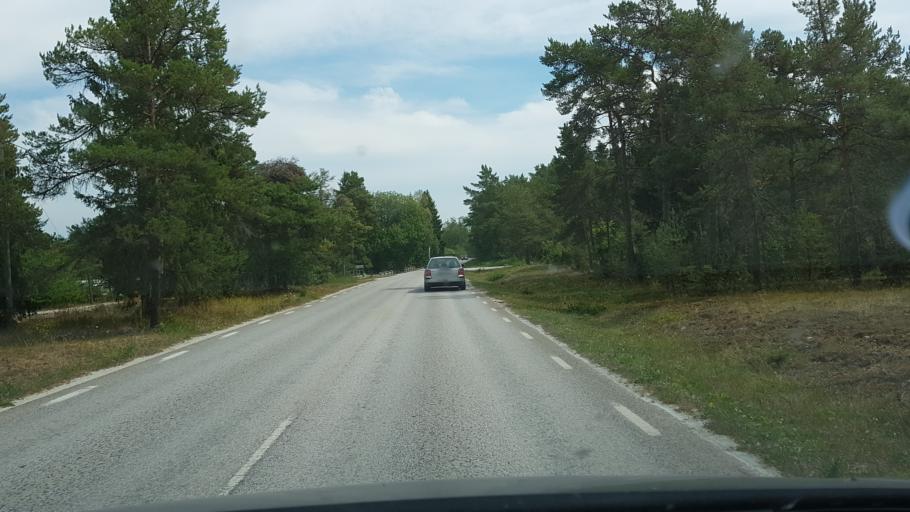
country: SE
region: Gotland
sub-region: Gotland
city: Slite
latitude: 57.7279
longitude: 18.7519
